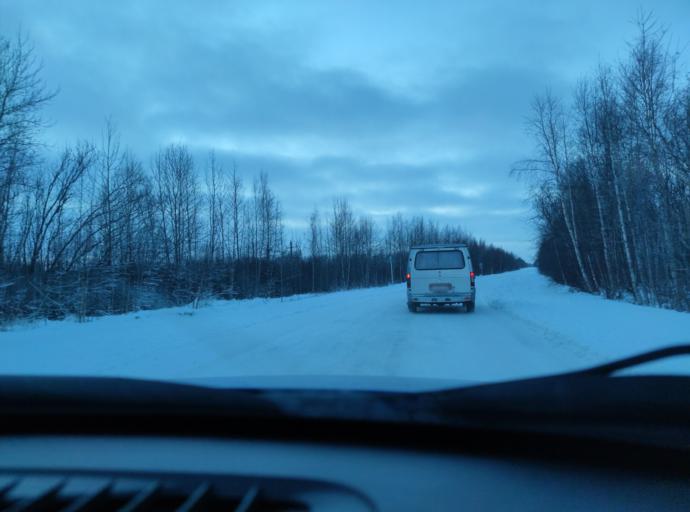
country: RU
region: Khanty-Mansiyskiy Avtonomnyy Okrug
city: Langepas
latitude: 61.1841
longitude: 75.1627
